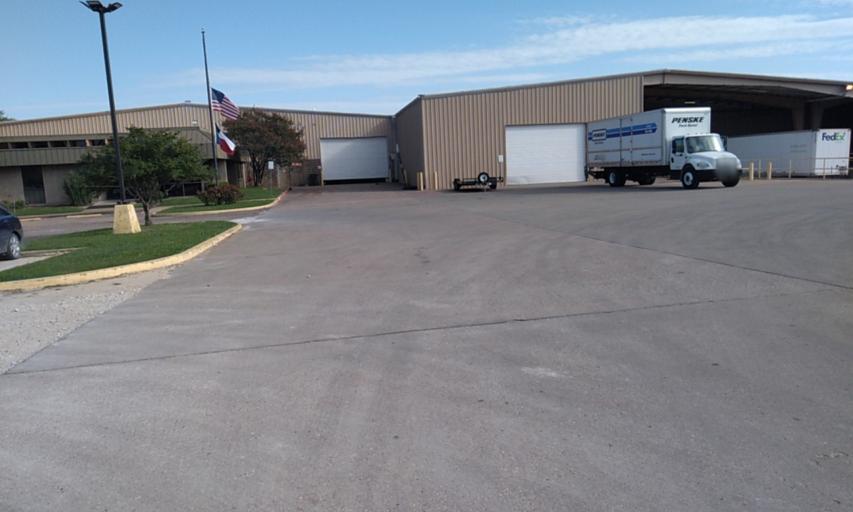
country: US
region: Texas
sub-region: McLennan County
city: Beverly Hills
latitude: 31.5238
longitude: -97.1619
